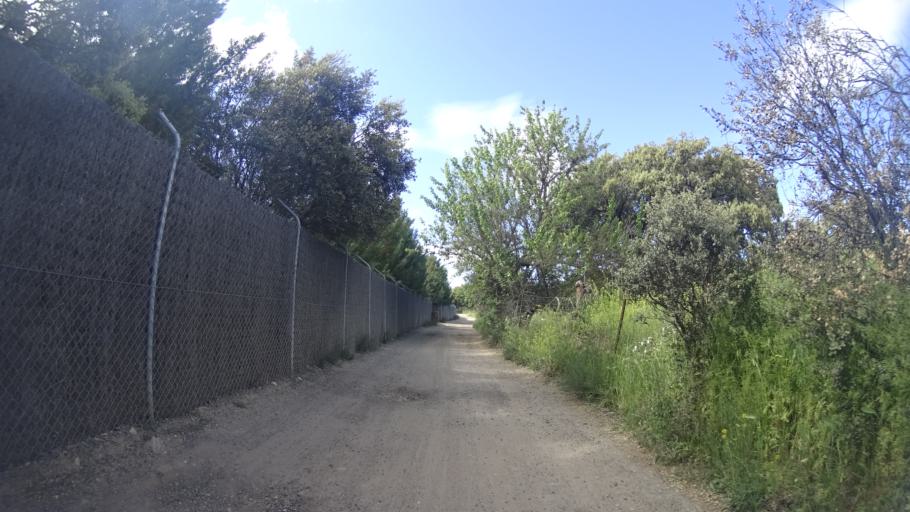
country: ES
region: Madrid
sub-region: Provincia de Madrid
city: Brunete
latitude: 40.4215
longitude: -3.9496
